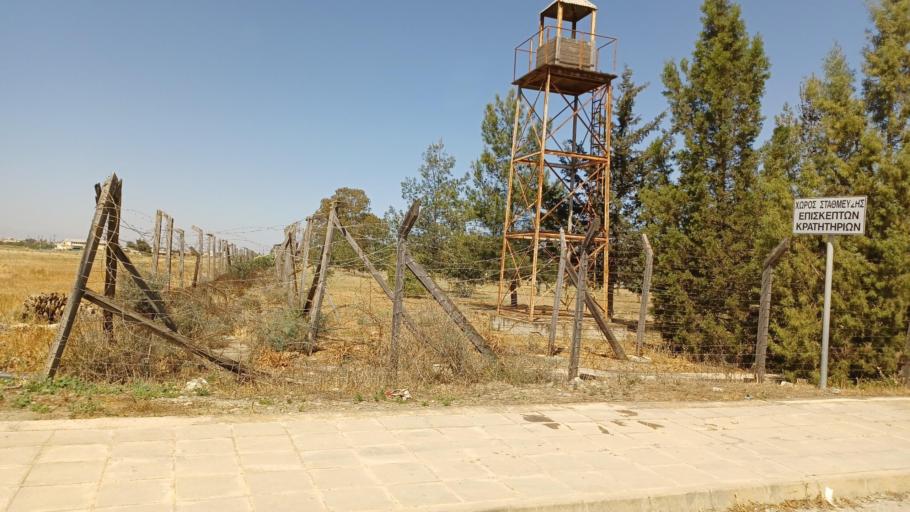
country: CY
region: Lefkosia
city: Kokkinotrimithia
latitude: 35.1531
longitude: 33.2249
